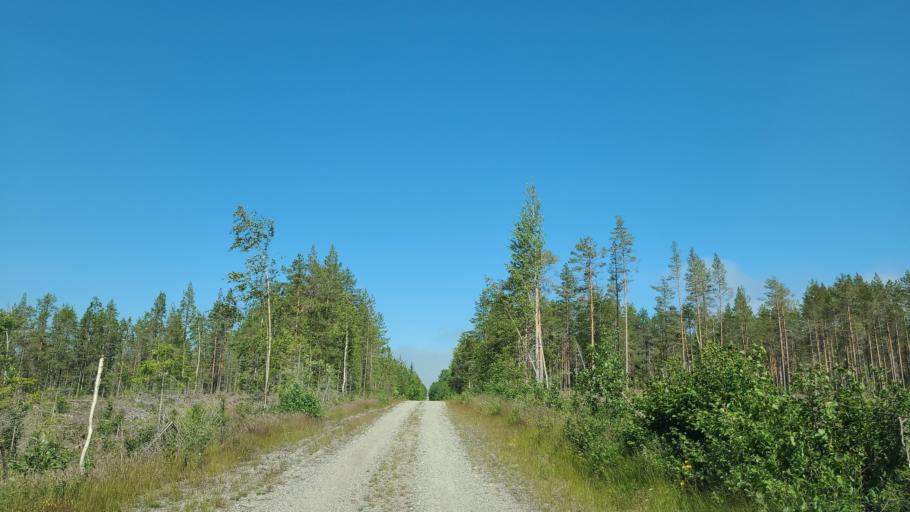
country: SE
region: Vaesternorrland
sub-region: OErnskoeldsviks Kommun
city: Husum
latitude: 63.4322
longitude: 19.2293
